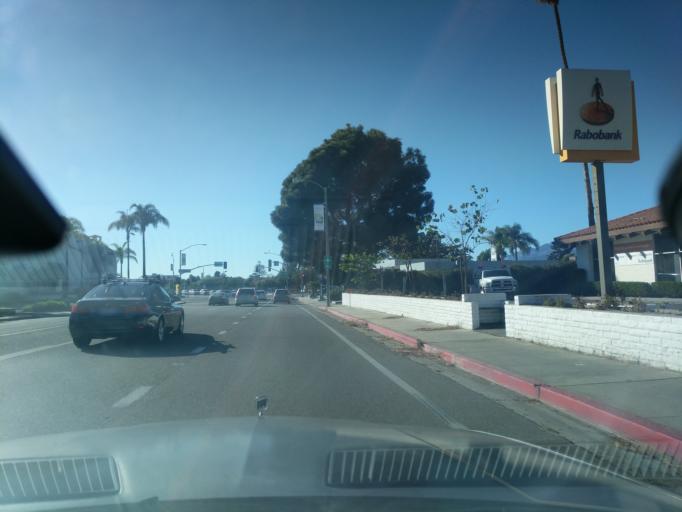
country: US
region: California
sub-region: Santa Barbara County
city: Goleta
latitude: 34.4417
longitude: -119.8295
